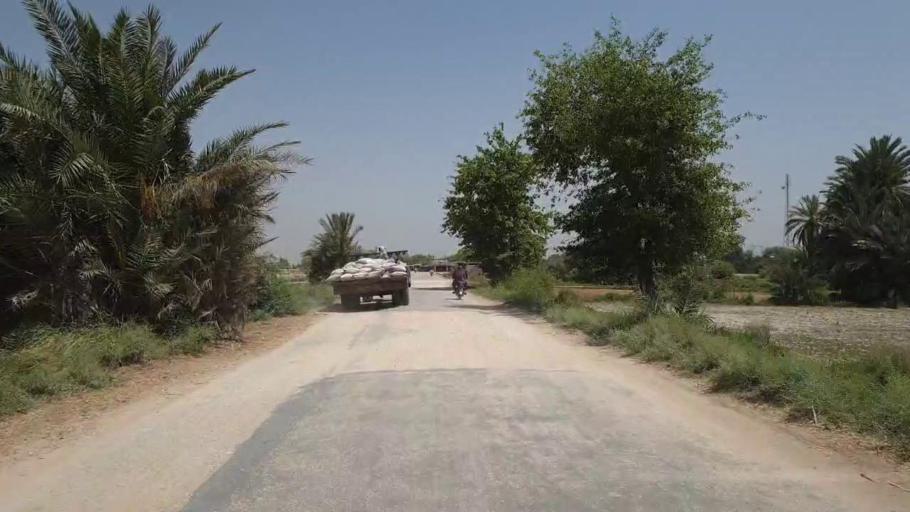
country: PK
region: Sindh
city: Adilpur
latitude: 27.8900
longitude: 69.2889
